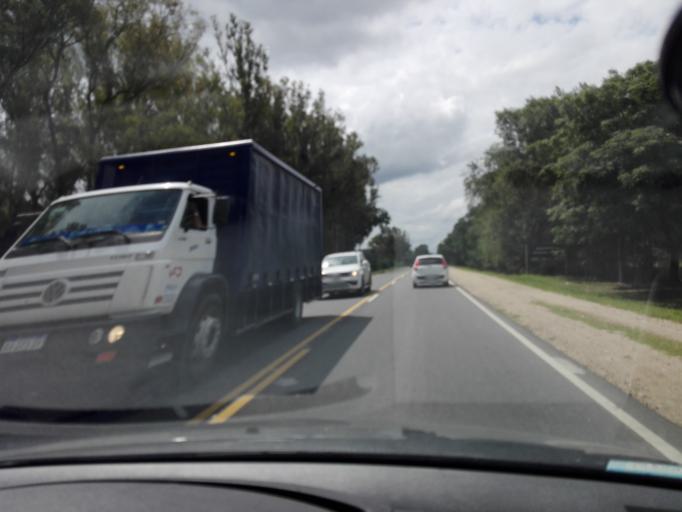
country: AR
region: Cordoba
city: Alta Gracia
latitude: -31.6015
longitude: -64.4503
